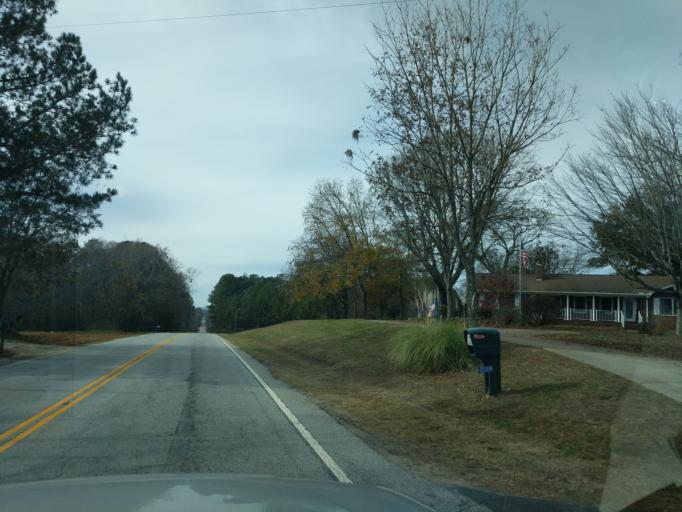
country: US
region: South Carolina
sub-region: Oconee County
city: Walhalla
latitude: 34.8056
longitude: -82.9785
